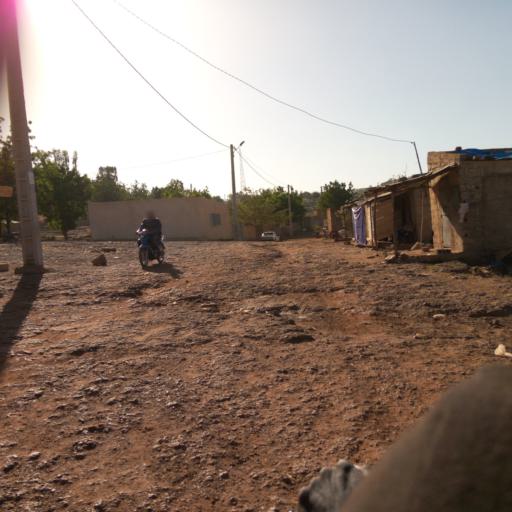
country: ML
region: Bamako
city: Bamako
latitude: 12.6557
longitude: -8.0392
